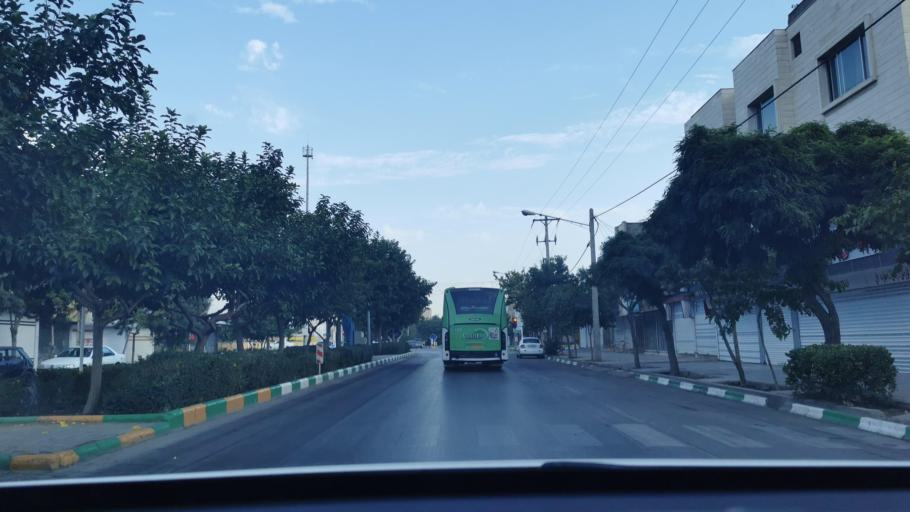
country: IR
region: Razavi Khorasan
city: Mashhad
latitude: 36.3557
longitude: 59.5266
